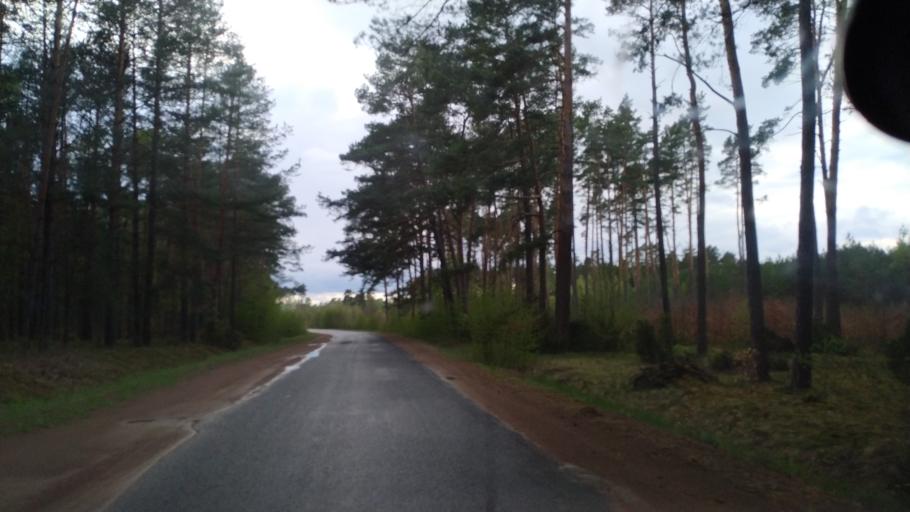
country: PL
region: Pomeranian Voivodeship
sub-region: Powiat starogardzki
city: Osiek
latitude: 53.6938
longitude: 18.5414
